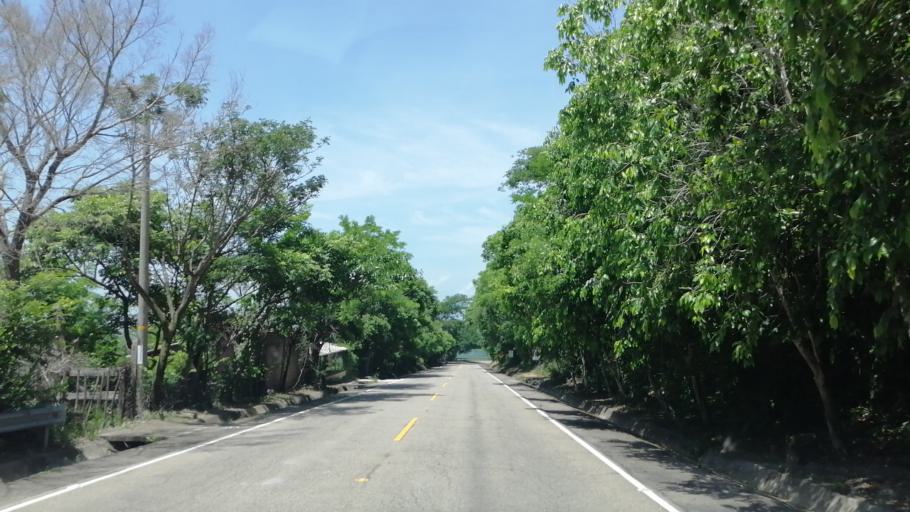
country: SV
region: Chalatenango
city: Nueva Concepcion
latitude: 14.1658
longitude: -89.3097
